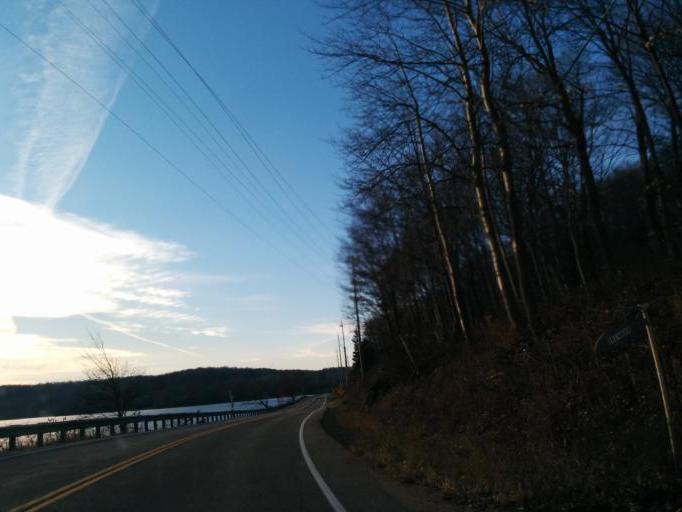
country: CA
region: Ontario
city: Bancroft
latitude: 45.0232
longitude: -78.3748
